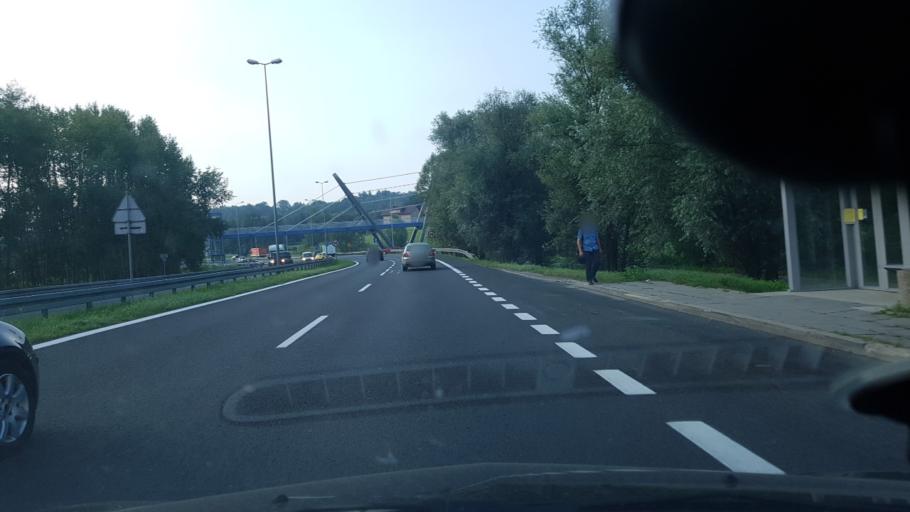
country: PL
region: Lesser Poland Voivodeship
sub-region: Powiat myslenicki
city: Glogoczow
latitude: 49.8941
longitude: 19.8738
